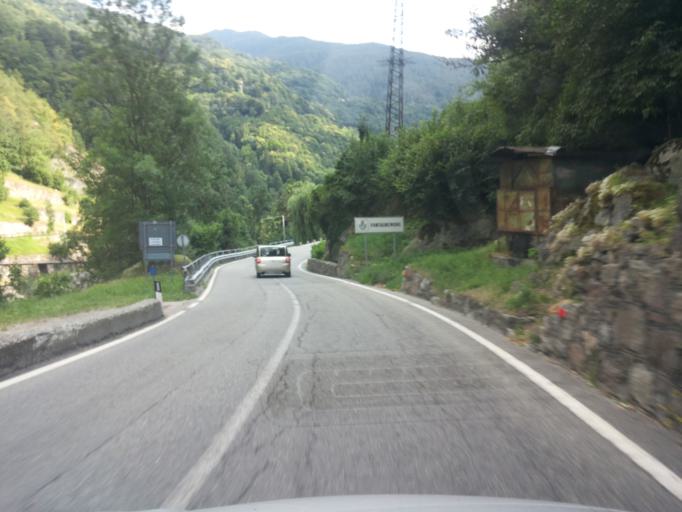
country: IT
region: Aosta Valley
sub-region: Valle d'Aosta
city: Fontainemore
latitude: 45.6543
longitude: 7.8599
